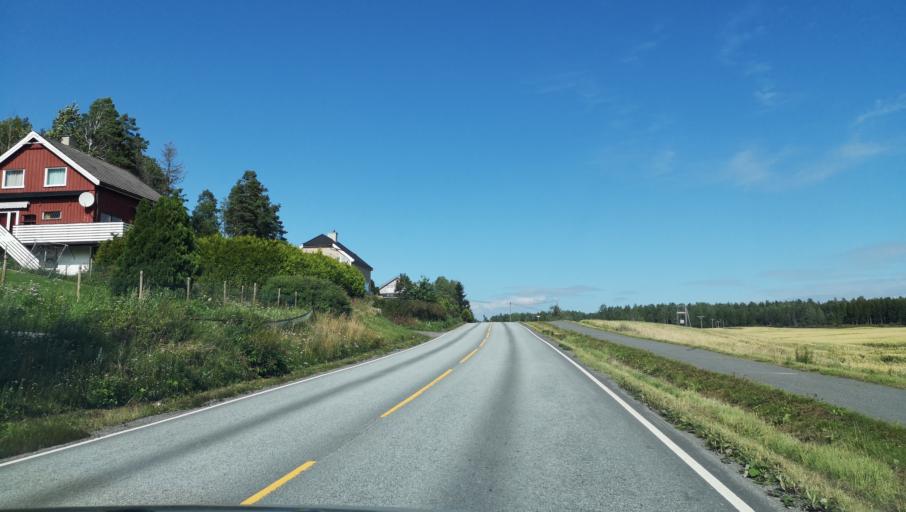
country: NO
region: Ostfold
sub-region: Valer
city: Kirkebygda
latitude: 59.5607
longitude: 10.8494
